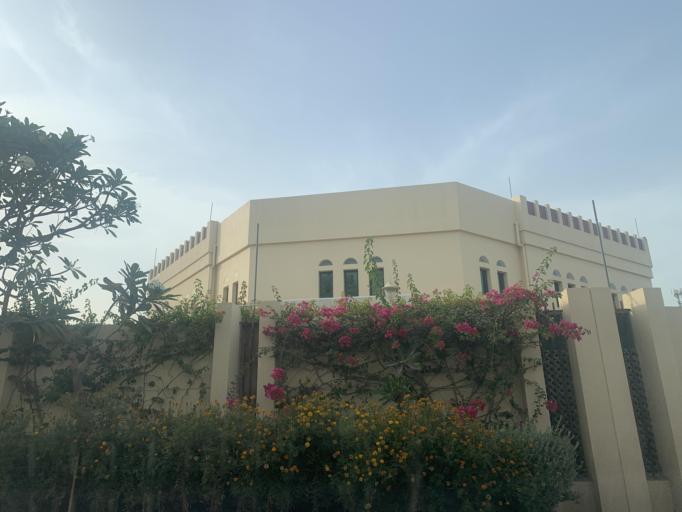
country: BH
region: Northern
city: Ar Rifa'
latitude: 26.1342
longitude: 50.5564
